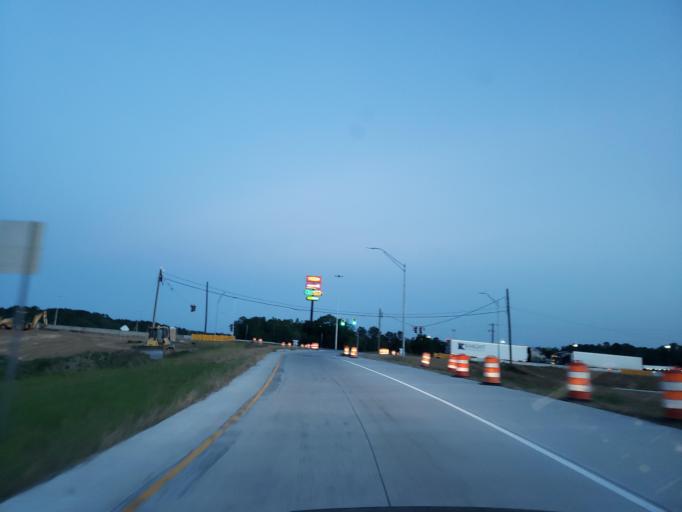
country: US
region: Georgia
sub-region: Echols County
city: Statenville
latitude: 30.6437
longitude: -83.1905
